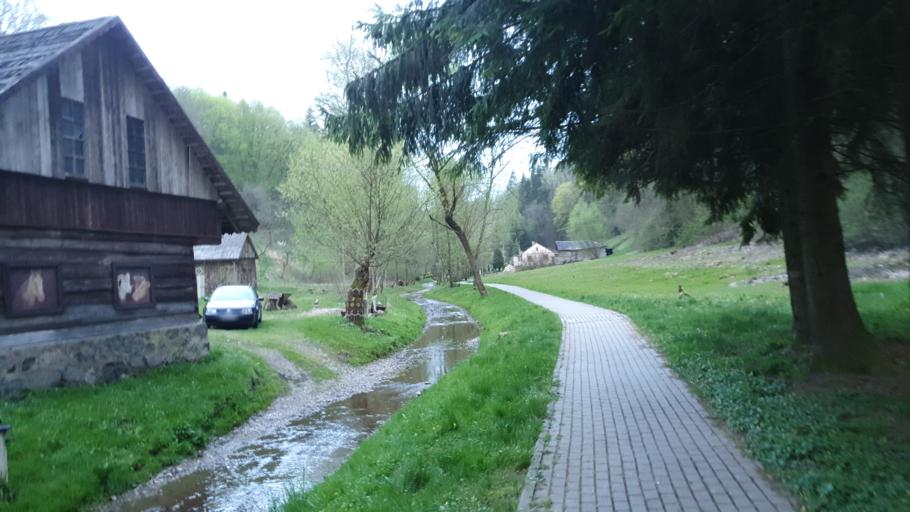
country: LT
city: Sakiai
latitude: 55.0820
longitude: 23.1779
